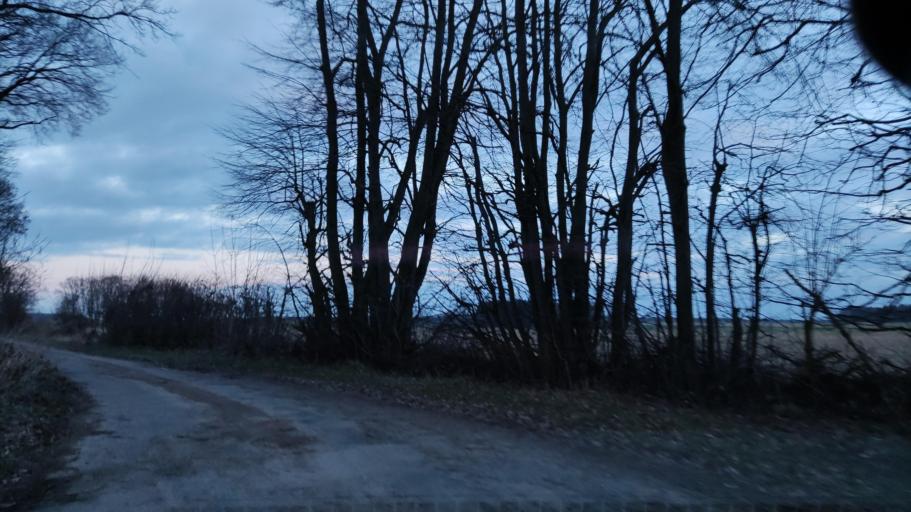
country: DE
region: Lower Saxony
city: Ebstorf
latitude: 53.0649
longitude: 10.4305
